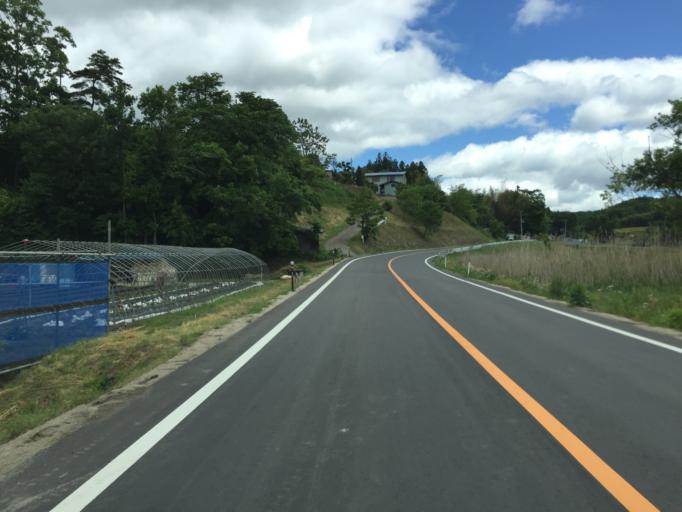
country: JP
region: Fukushima
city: Motomiya
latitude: 37.5140
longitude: 140.4430
